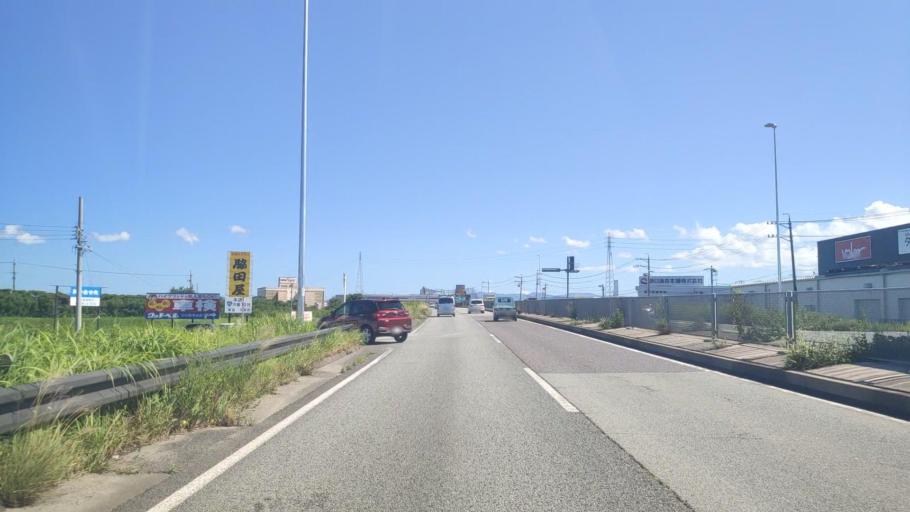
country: JP
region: Mie
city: Hisai-motomachi
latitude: 34.6095
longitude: 136.5190
